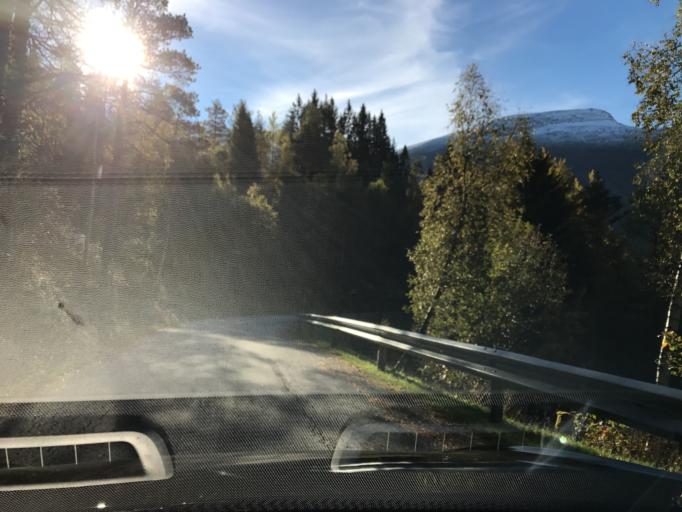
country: NO
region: More og Romsdal
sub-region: Norddal
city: Valldal
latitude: 62.3362
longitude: 7.3901
